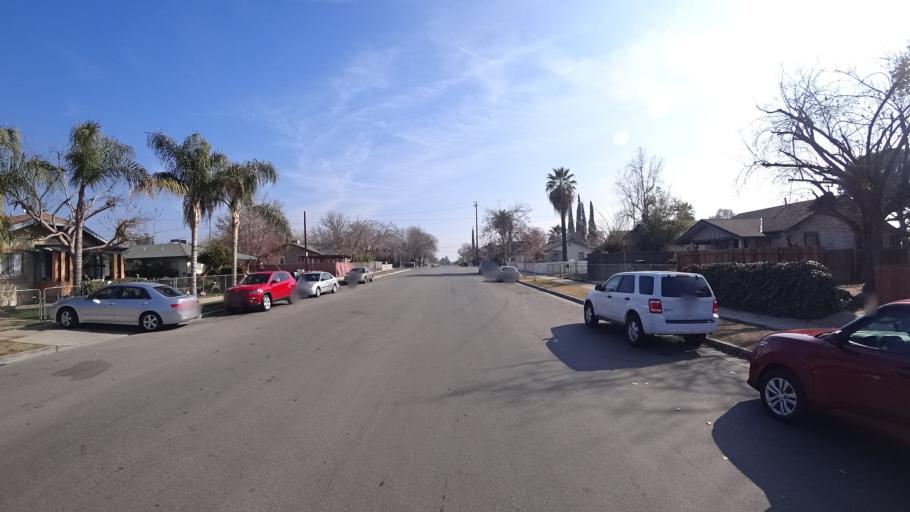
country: US
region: California
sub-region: Kern County
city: Bakersfield
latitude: 35.3875
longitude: -118.9902
